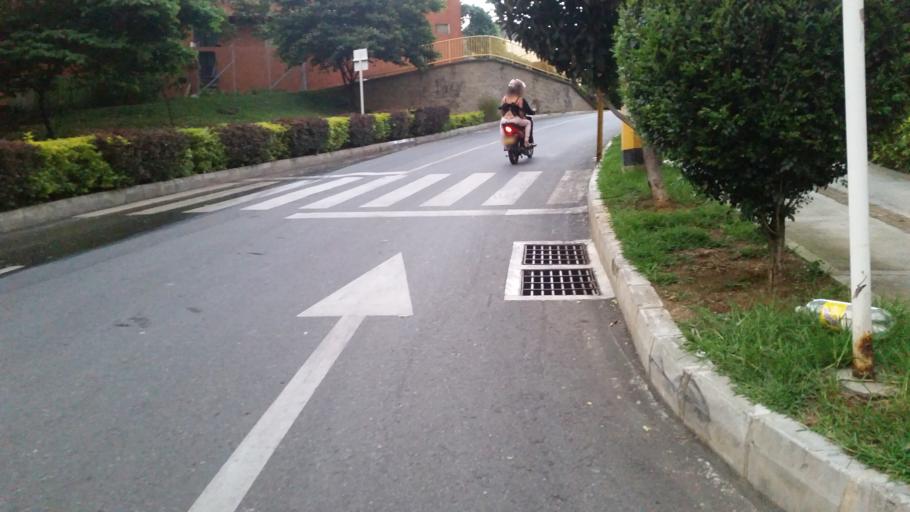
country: CO
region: Antioquia
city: Medellin
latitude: 6.2812
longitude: -75.5781
